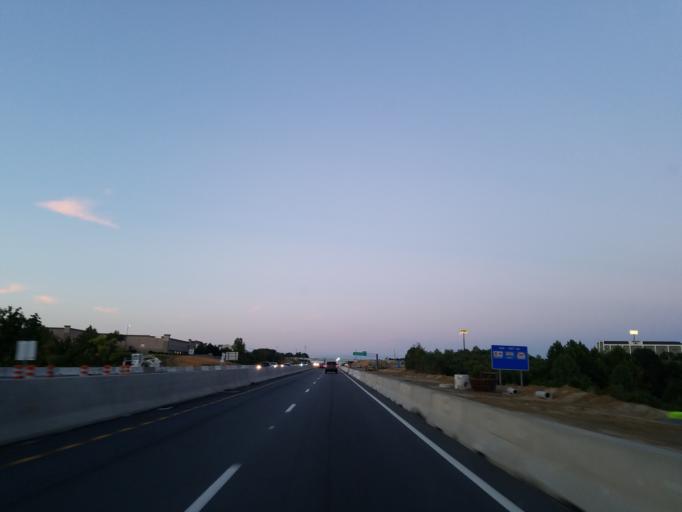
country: US
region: North Carolina
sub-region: Cabarrus County
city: Kannapolis
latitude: 35.4596
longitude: -80.5909
